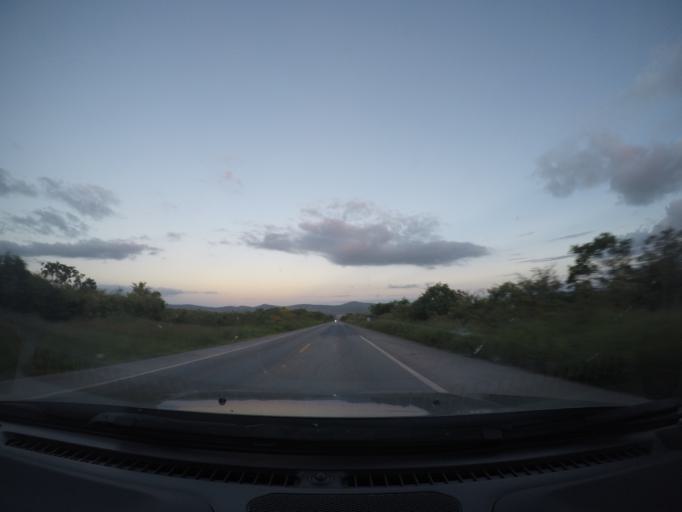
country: BR
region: Bahia
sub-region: Seabra
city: Seabra
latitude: -12.4309
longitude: -41.7964
